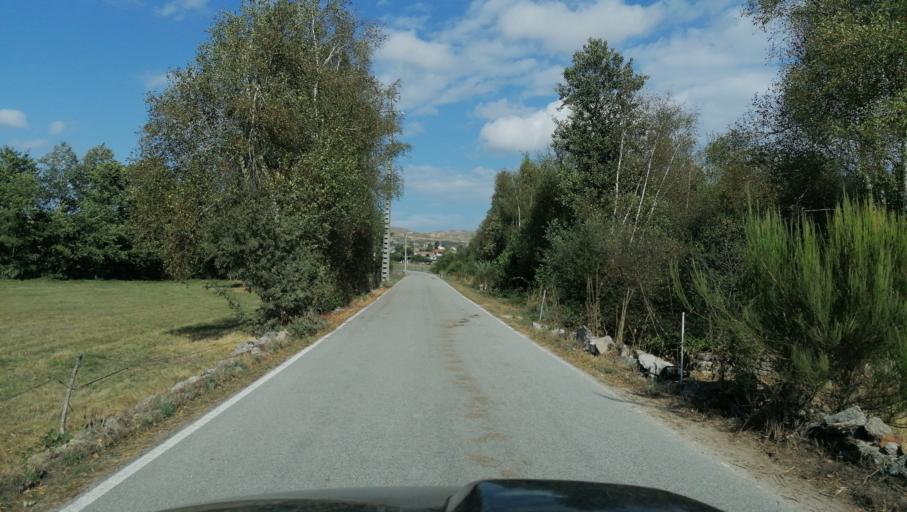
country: PT
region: Vila Real
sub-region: Vila Pouca de Aguiar
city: Vila Pouca de Aguiar
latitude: 41.5196
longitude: -7.6672
